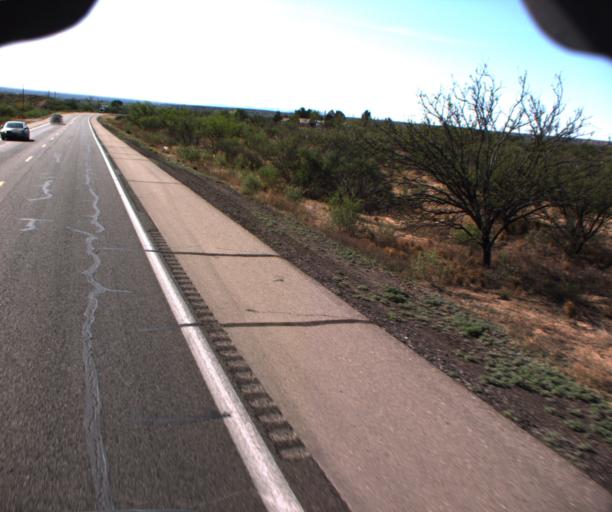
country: US
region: Arizona
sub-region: Cochise County
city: Benson
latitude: 31.9209
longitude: -110.2682
